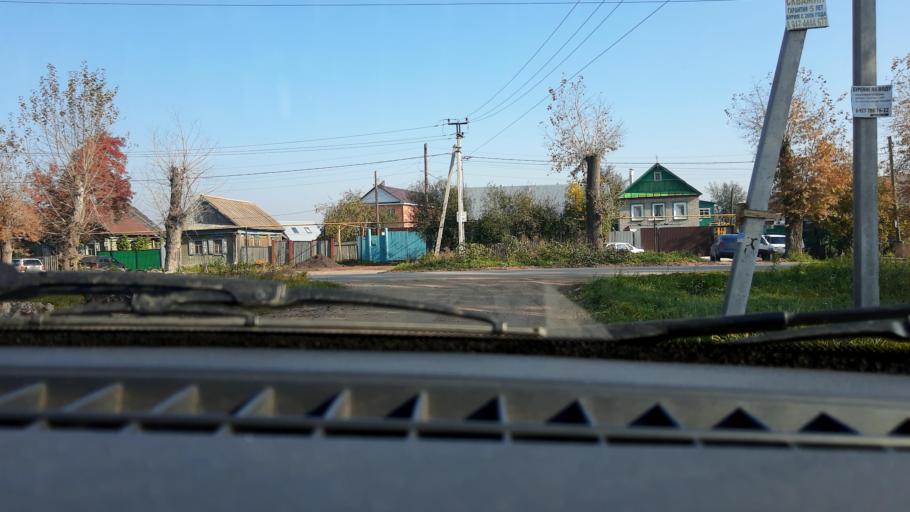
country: RU
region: Bashkortostan
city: Mikhaylovka
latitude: 54.7596
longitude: 55.9025
